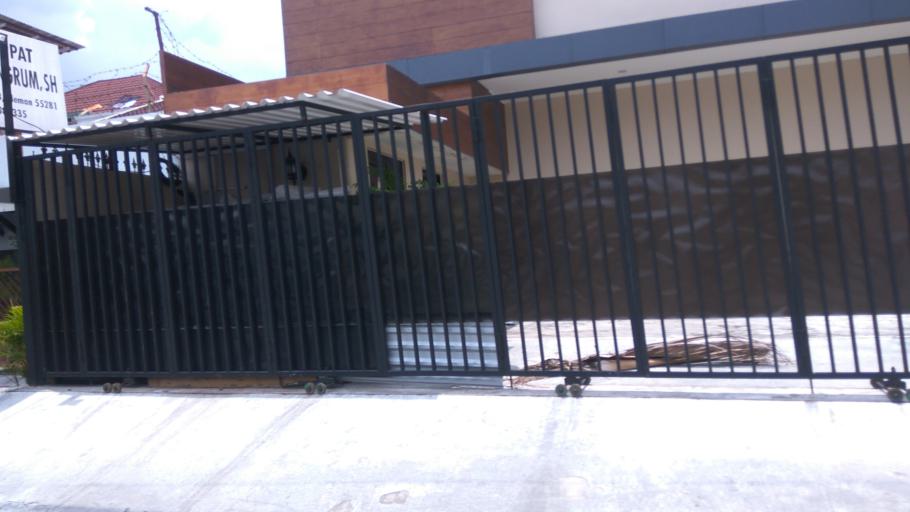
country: ID
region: Daerah Istimewa Yogyakarta
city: Yogyakarta
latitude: -7.7630
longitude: 110.3894
